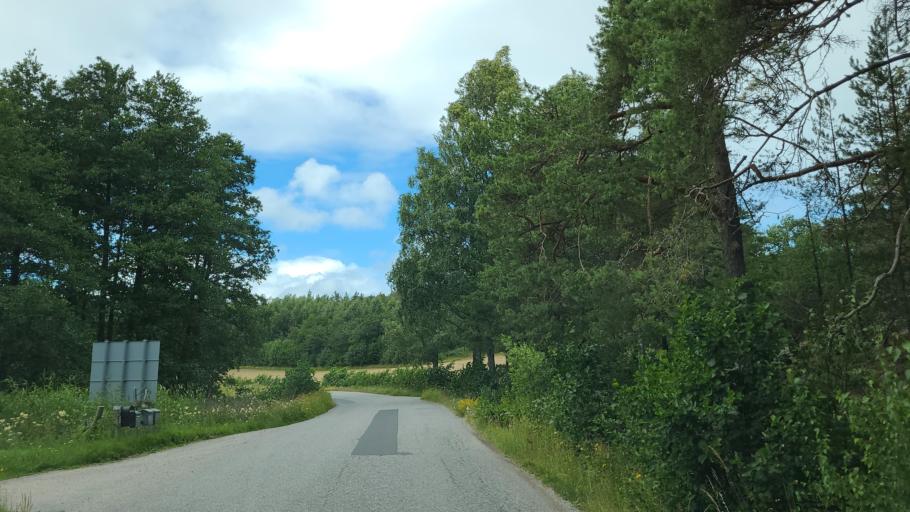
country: FI
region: Varsinais-Suomi
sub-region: Aboland-Turunmaa
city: Nagu
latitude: 60.1648
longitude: 22.0001
